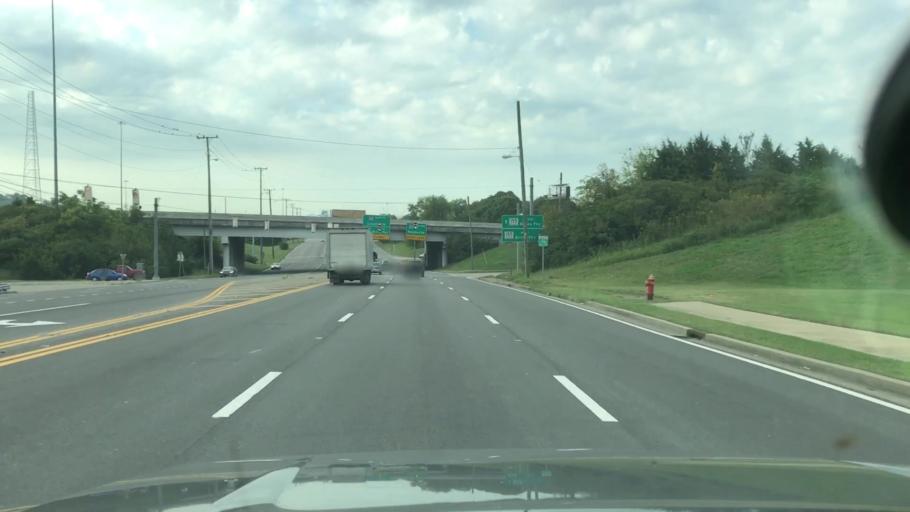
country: US
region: Tennessee
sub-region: Davidson County
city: Nashville
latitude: 36.2429
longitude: -86.7570
